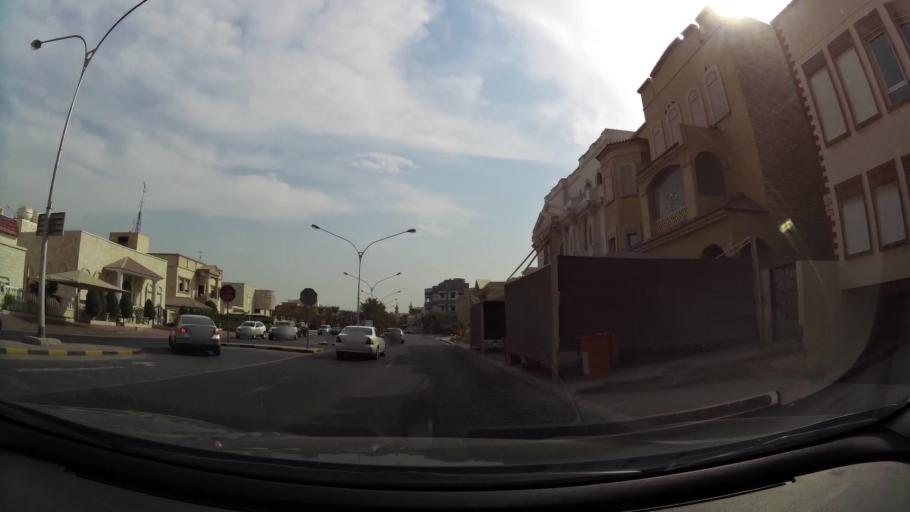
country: KW
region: Al Asimah
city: Ash Shamiyah
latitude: 29.3150
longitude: 47.9682
